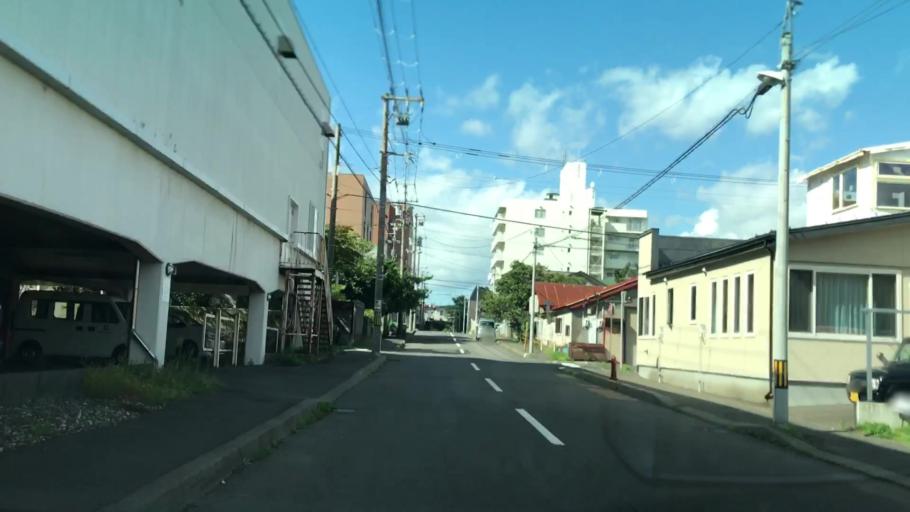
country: JP
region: Hokkaido
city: Muroran
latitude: 42.3144
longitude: 140.9711
